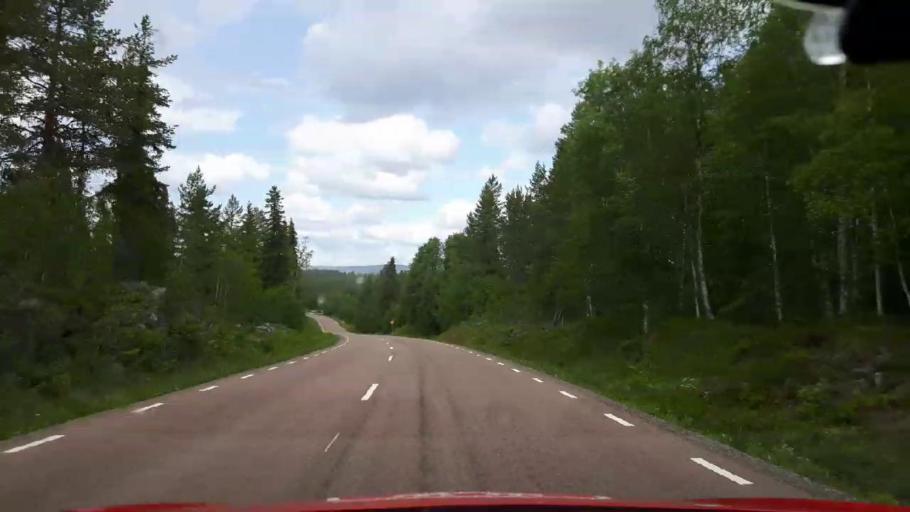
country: SE
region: Jaemtland
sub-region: Krokoms Kommun
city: Valla
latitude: 63.9423
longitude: 14.2249
